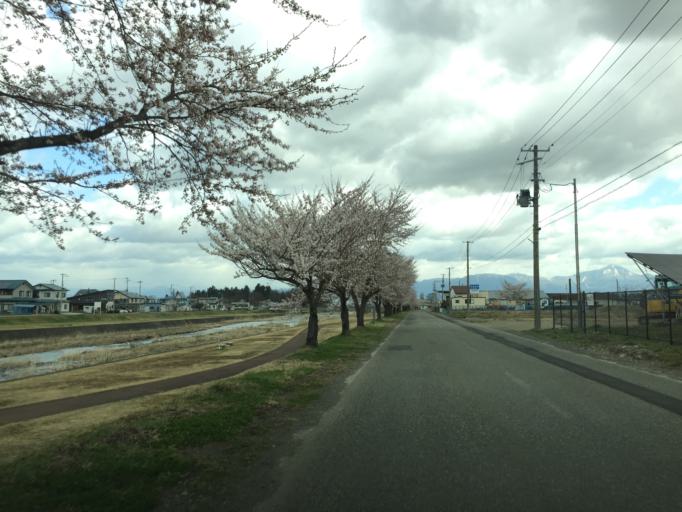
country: JP
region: Fukushima
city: Kitakata
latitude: 37.4490
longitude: 139.8376
